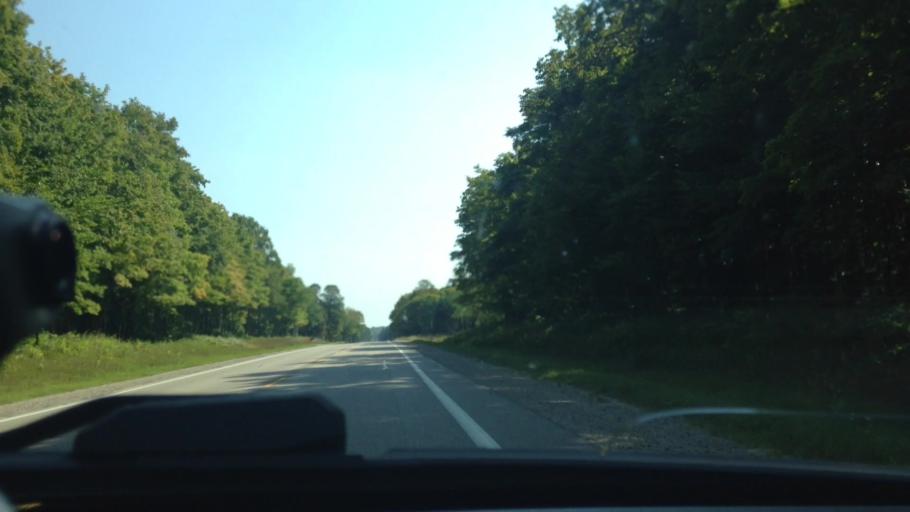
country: US
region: Michigan
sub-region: Luce County
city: Newberry
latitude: 46.3218
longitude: -85.6685
